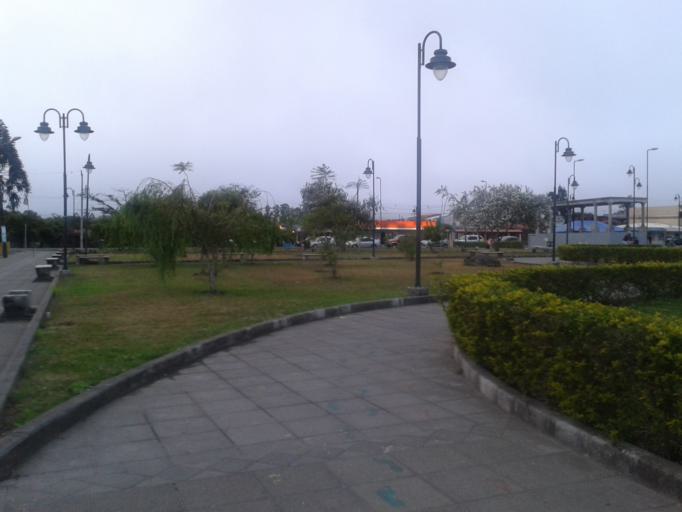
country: CR
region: Cartago
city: Cartago
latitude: 9.8442
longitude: -83.9386
